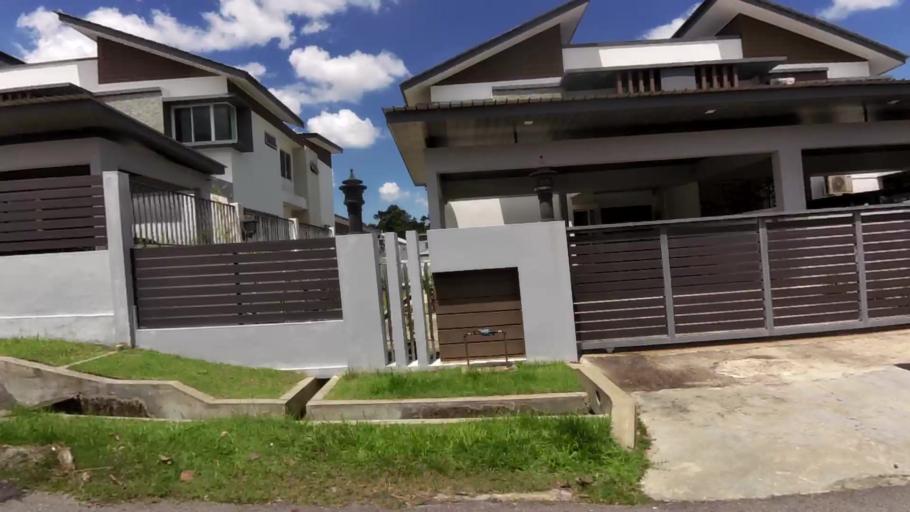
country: BN
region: Brunei and Muara
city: Bandar Seri Begawan
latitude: 4.9442
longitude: 114.9617
